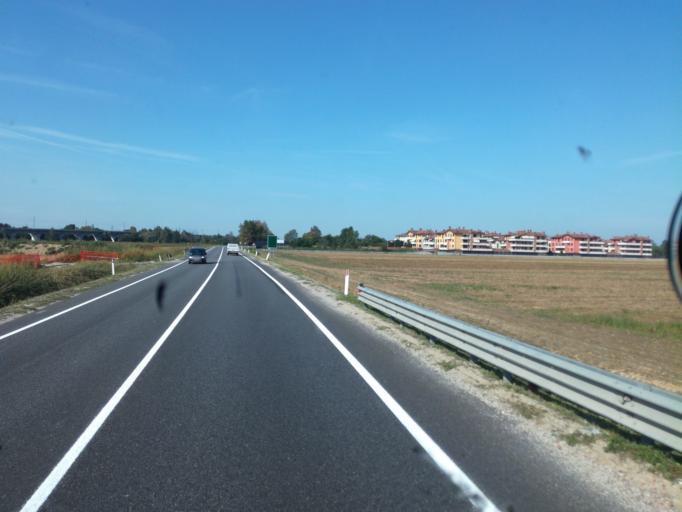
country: IT
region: Lombardy
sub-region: Provincia di Lodi
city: Sordio
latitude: 45.3359
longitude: 9.3769
